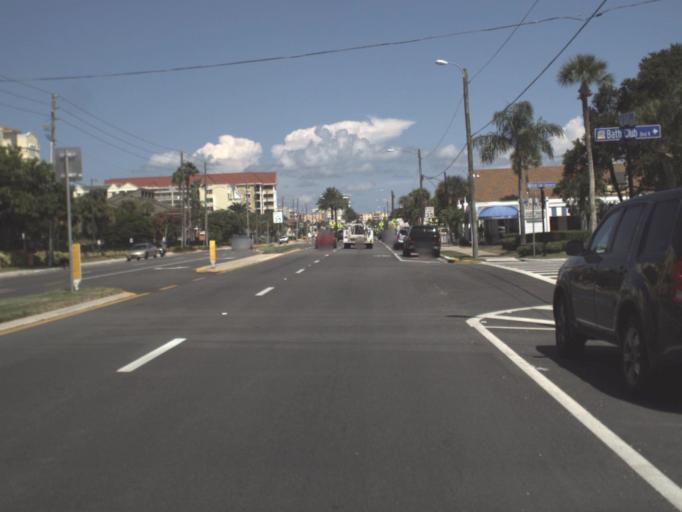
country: US
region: Florida
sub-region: Pinellas County
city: North Redington Beach
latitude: 27.8160
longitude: -82.8209
